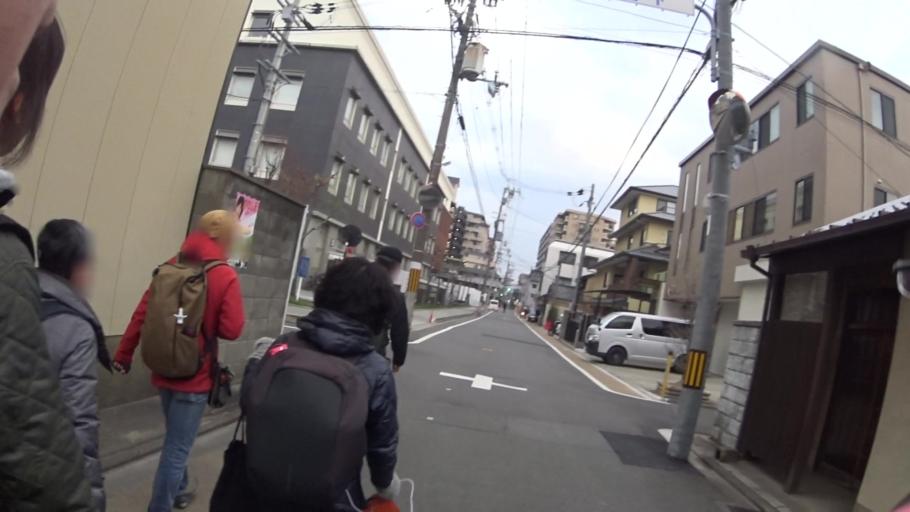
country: JP
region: Kyoto
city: Uji
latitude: 34.9366
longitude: 135.7610
